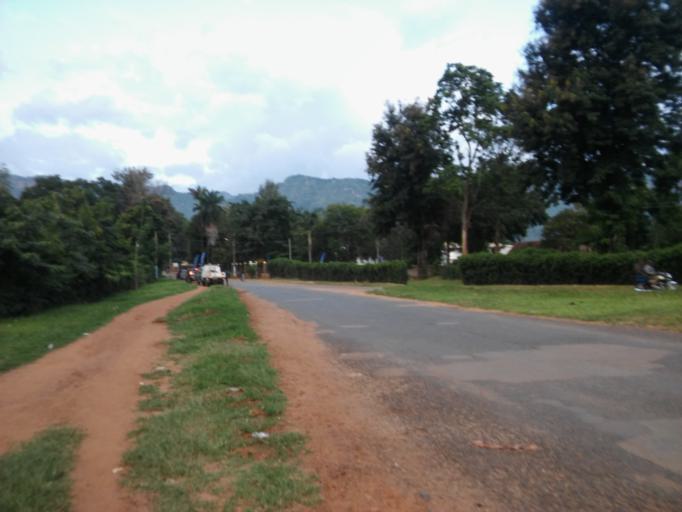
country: UG
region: Eastern Region
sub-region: Mbale District
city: Mbale
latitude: 1.0671
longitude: 34.1936
